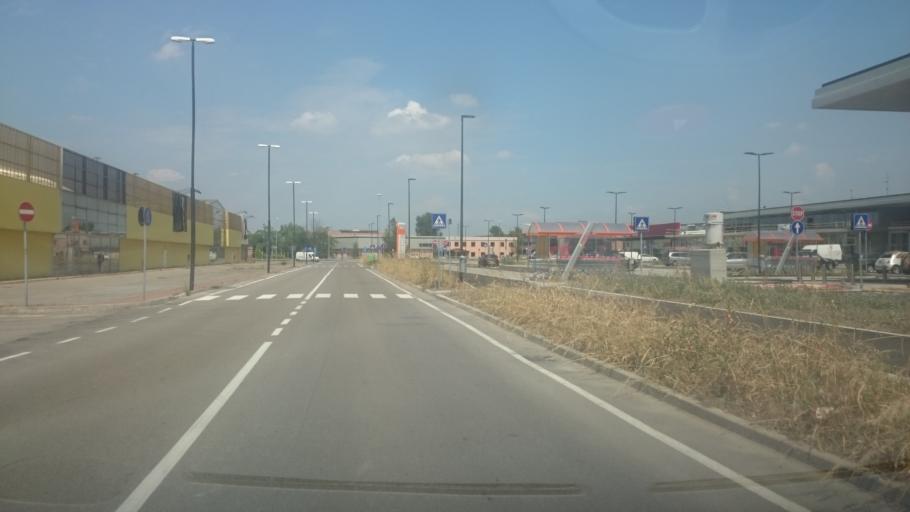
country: IT
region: Emilia-Romagna
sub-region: Provincia di Reggio Emilia
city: Bagno
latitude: 44.6536
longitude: 10.7661
